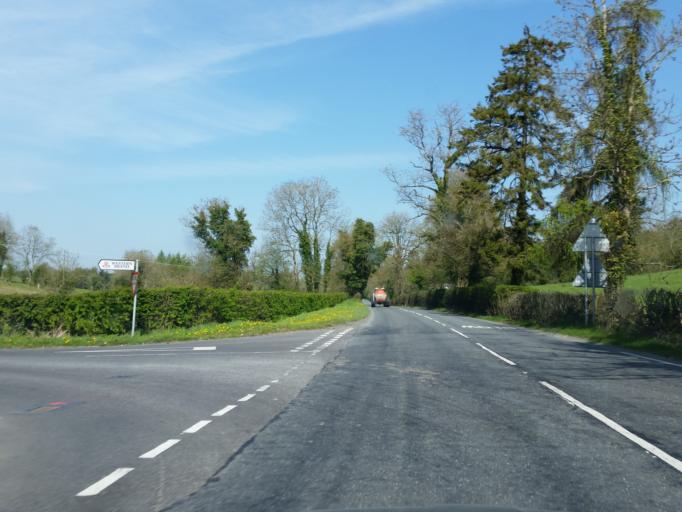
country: GB
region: Northern Ireland
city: Lisnaskea
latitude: 54.2230
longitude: -7.4126
